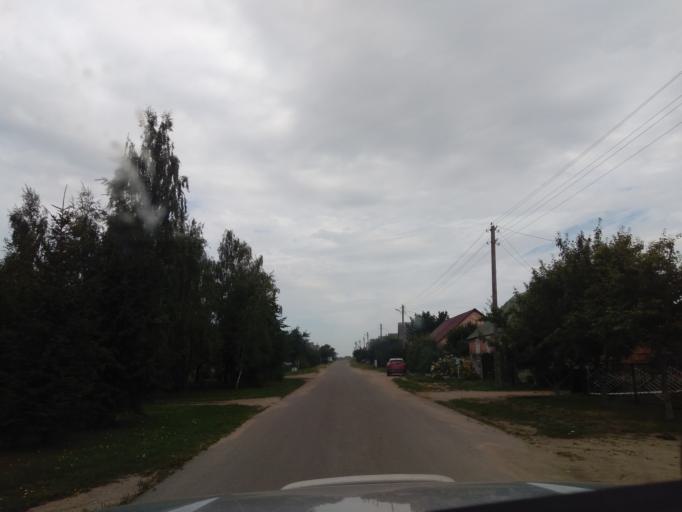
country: BY
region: Minsk
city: Kapyl'
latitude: 53.1559
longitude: 27.0696
